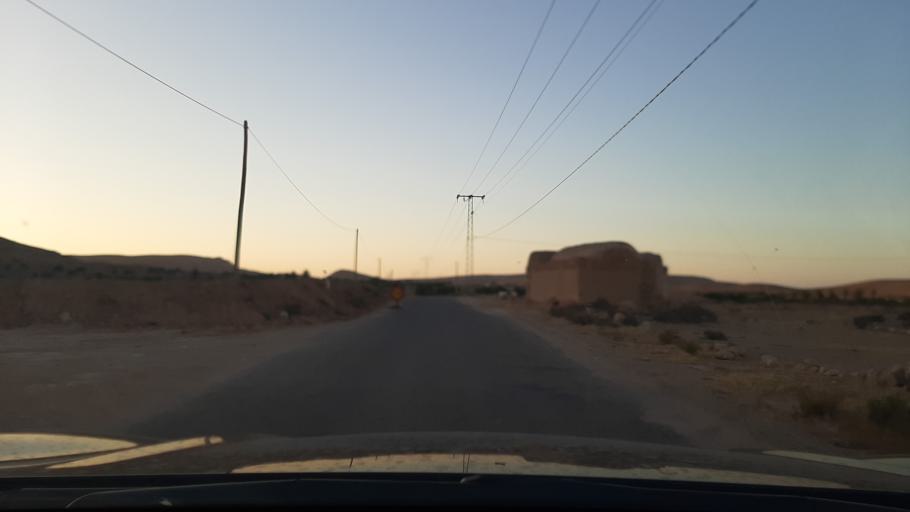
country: TN
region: Qabis
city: Matmata
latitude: 33.5503
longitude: 10.1886
